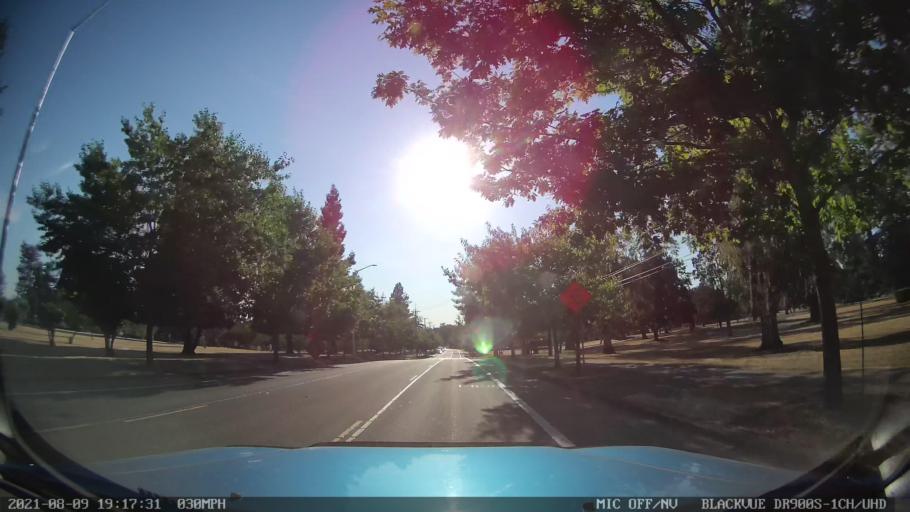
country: US
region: Oregon
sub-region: Marion County
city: Four Corners
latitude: 44.9400
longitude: -123.0047
